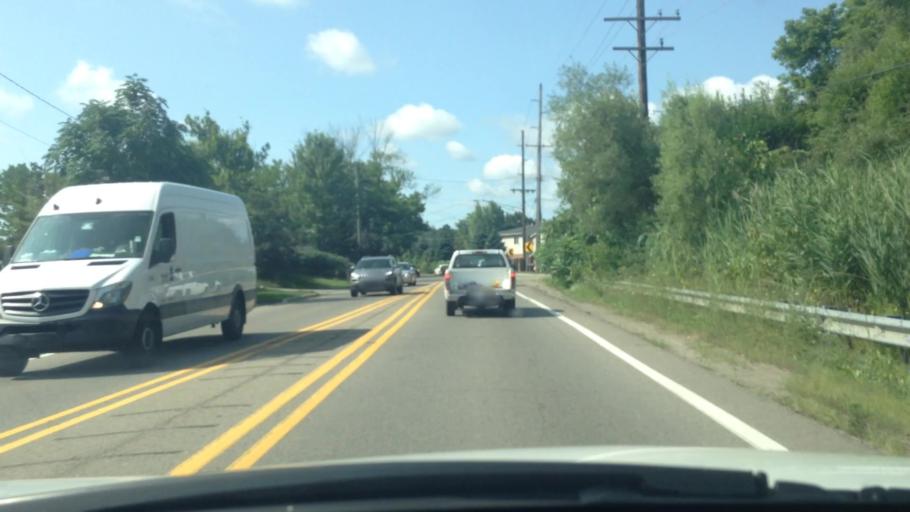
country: US
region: Michigan
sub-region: Oakland County
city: Wolverine Lake
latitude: 42.5860
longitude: -83.4461
